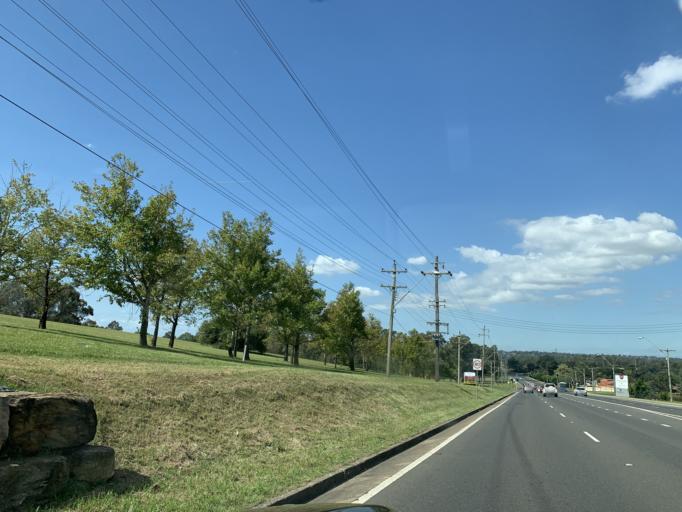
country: AU
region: New South Wales
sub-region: Penrith Municipality
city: Werrington County
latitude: -33.7642
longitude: 150.7433
